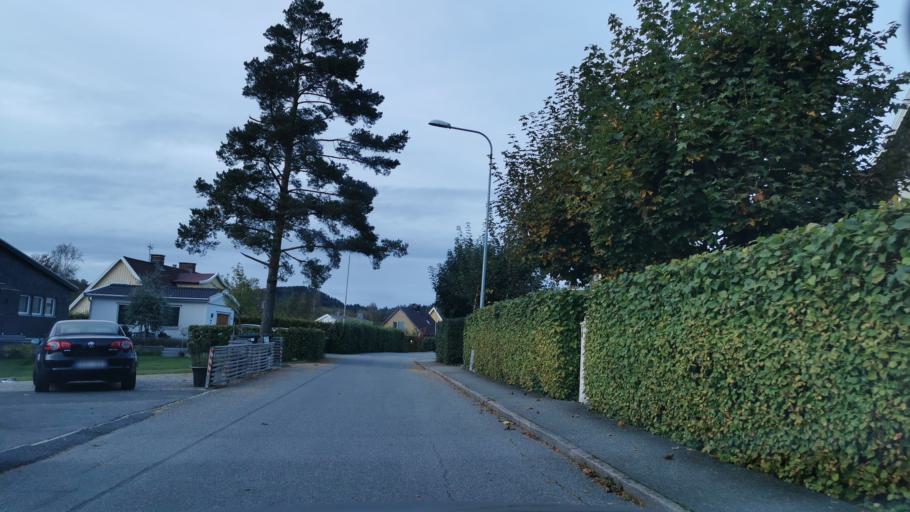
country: SE
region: Vaestra Goetaland
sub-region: Goteborg
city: Eriksbo
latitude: 57.7381
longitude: 12.0447
